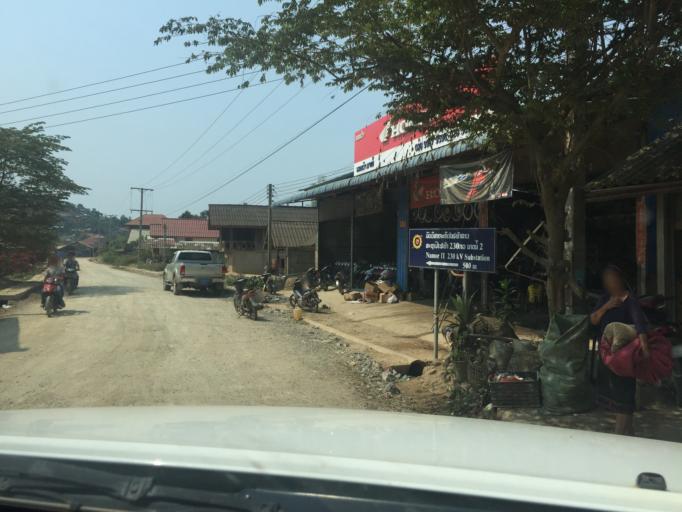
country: LA
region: Oudomxai
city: Muang Xay
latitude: 20.9064
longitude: 101.7614
